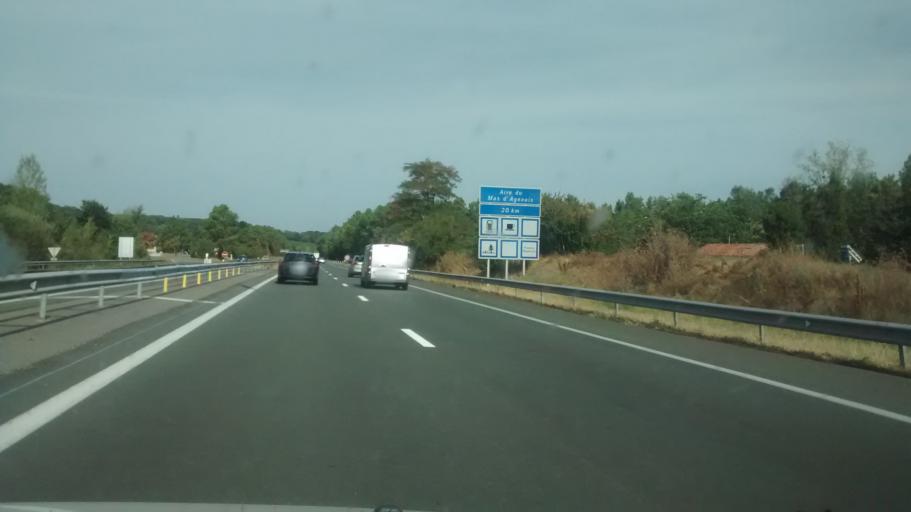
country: FR
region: Aquitaine
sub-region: Departement du Lot-et-Garonne
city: Buzet-sur-Baise
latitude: 44.2482
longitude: 0.3044
